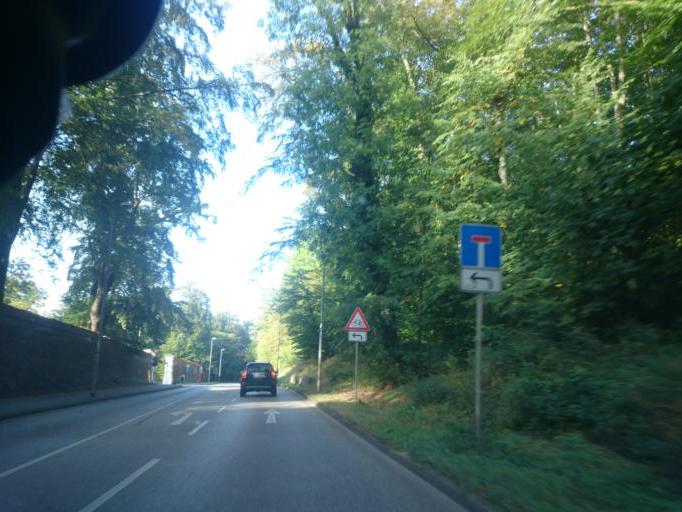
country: DE
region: Mecklenburg-Vorpommern
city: Bad Doberan
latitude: 54.1064
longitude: 11.9118
